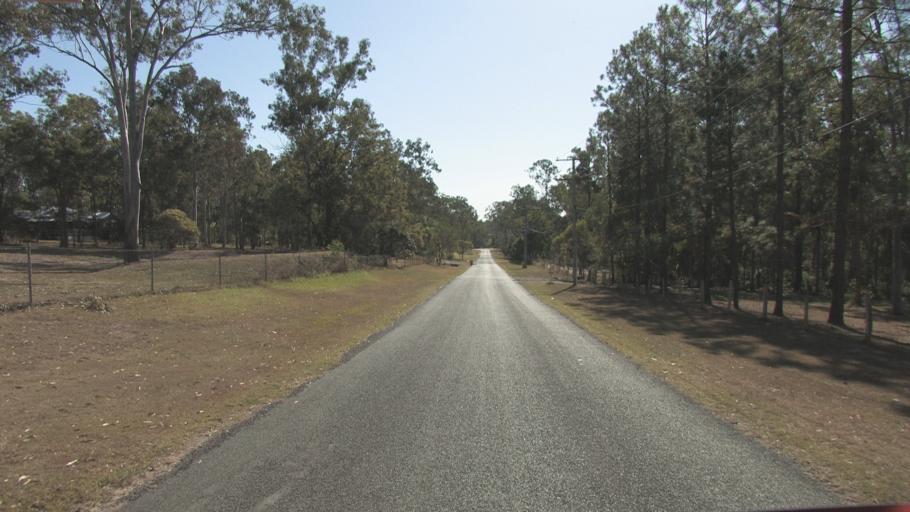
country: AU
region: Queensland
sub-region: Logan
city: Cedar Vale
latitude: -27.8276
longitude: 153.0478
